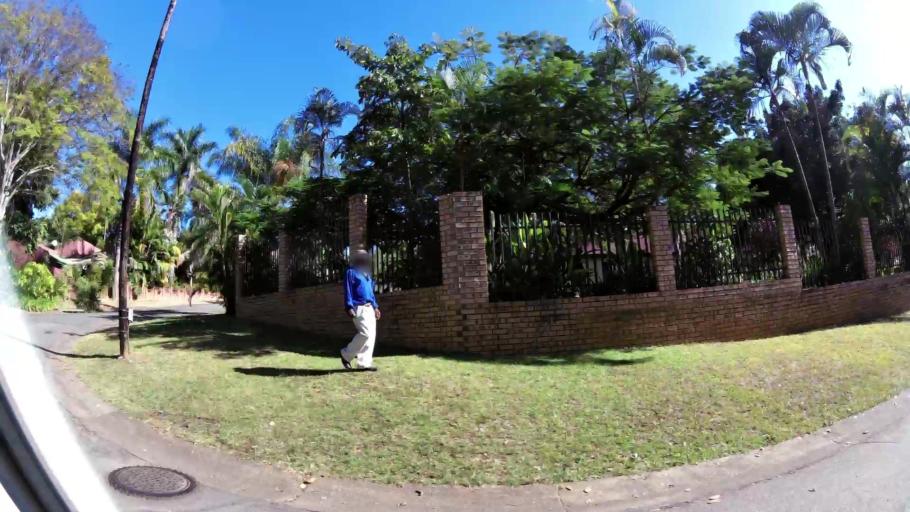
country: ZA
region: Limpopo
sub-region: Mopani District Municipality
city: Tzaneen
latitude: -23.8290
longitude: 30.1471
